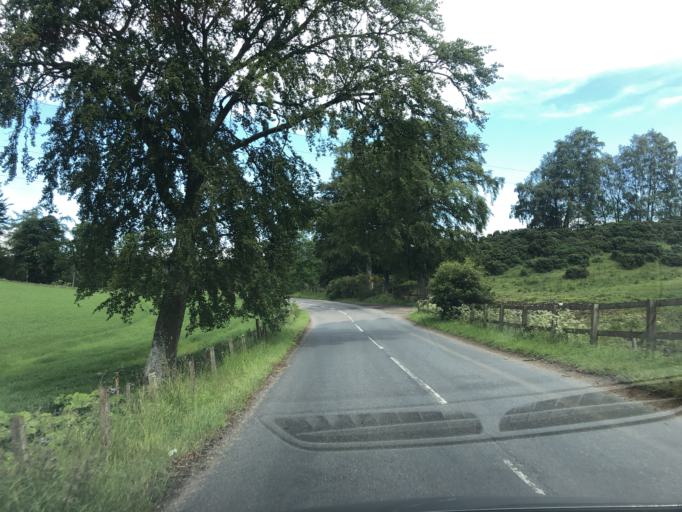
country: GB
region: Scotland
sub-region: Angus
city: Kirriemuir
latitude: 56.7108
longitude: -2.9798
